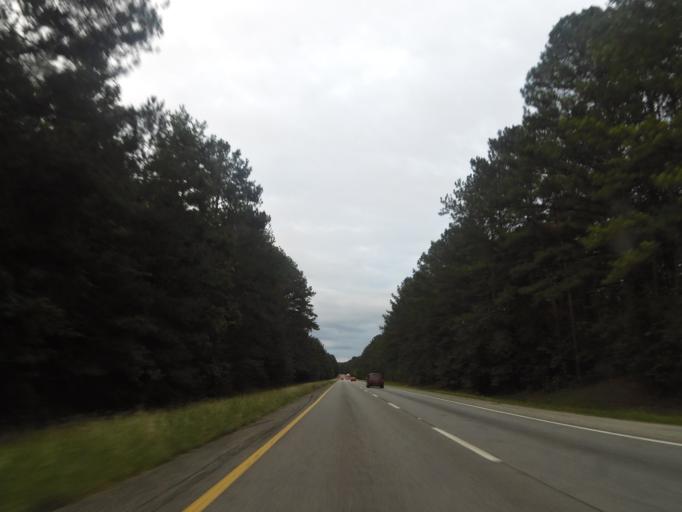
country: US
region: Alabama
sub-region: Saint Clair County
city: Springville
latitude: 33.7832
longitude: -86.4040
